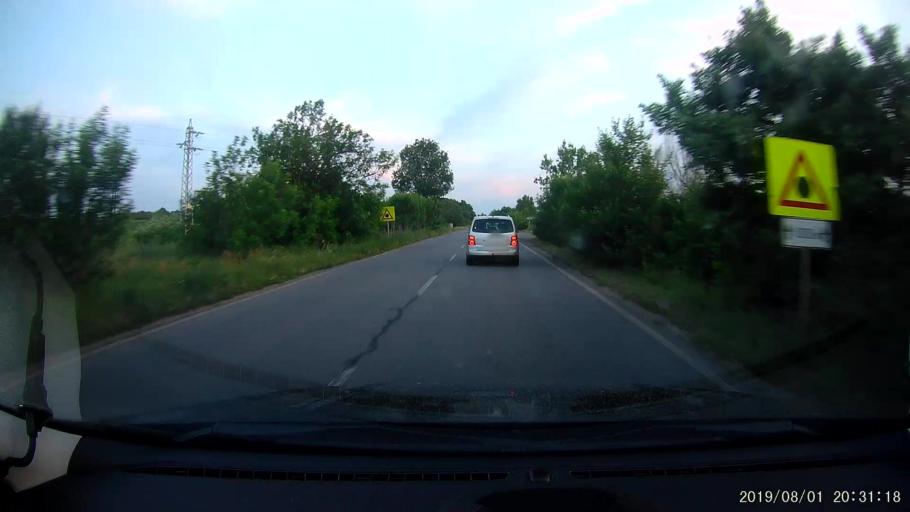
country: BG
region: Yambol
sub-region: Obshtina Elkhovo
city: Elkhovo
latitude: 42.1299
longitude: 26.5405
